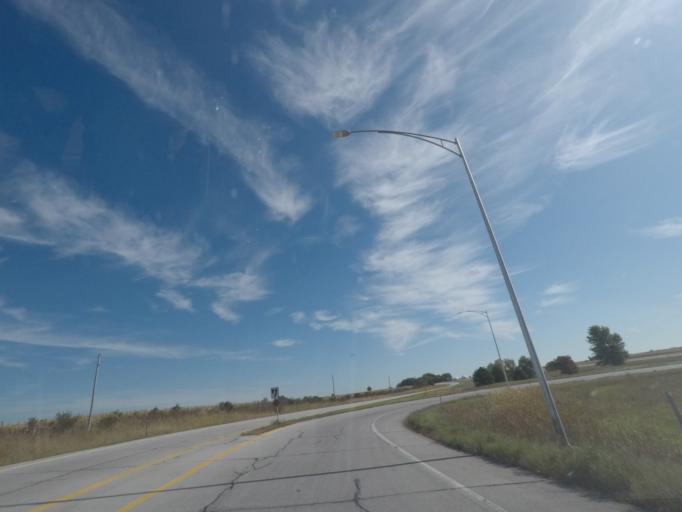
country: US
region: Iowa
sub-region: Marshall County
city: State Center
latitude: 42.0091
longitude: -93.3078
